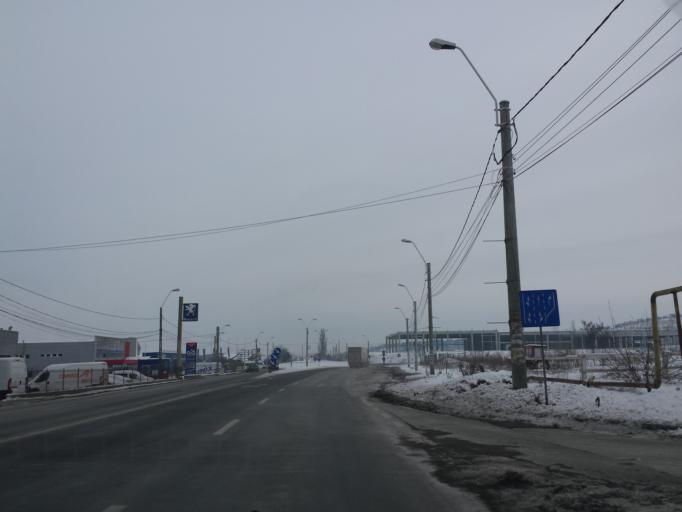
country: RO
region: Hunedoara
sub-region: Municipiul Deva
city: Cristur
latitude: 45.8588
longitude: 22.9388
